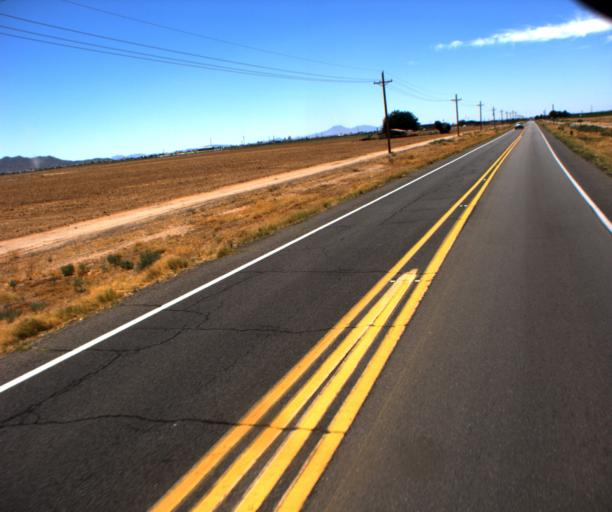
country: US
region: Arizona
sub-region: Pinal County
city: Casa Grande
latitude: 32.8797
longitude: -111.6557
